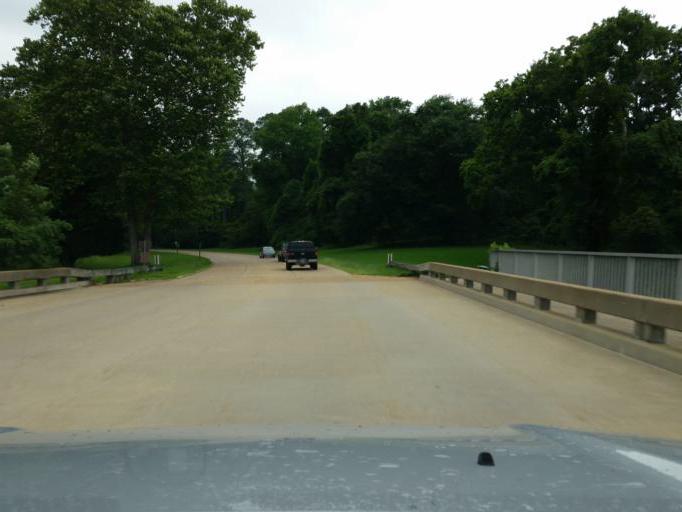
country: US
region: Virginia
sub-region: York County
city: Yorktown
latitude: 37.2741
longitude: -76.5862
